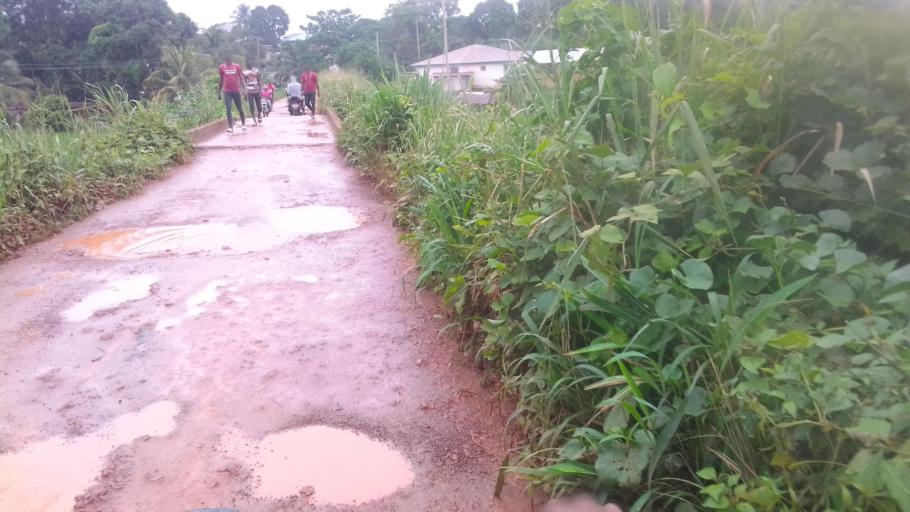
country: SL
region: Eastern Province
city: Kenema
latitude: 7.8876
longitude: -11.1778
